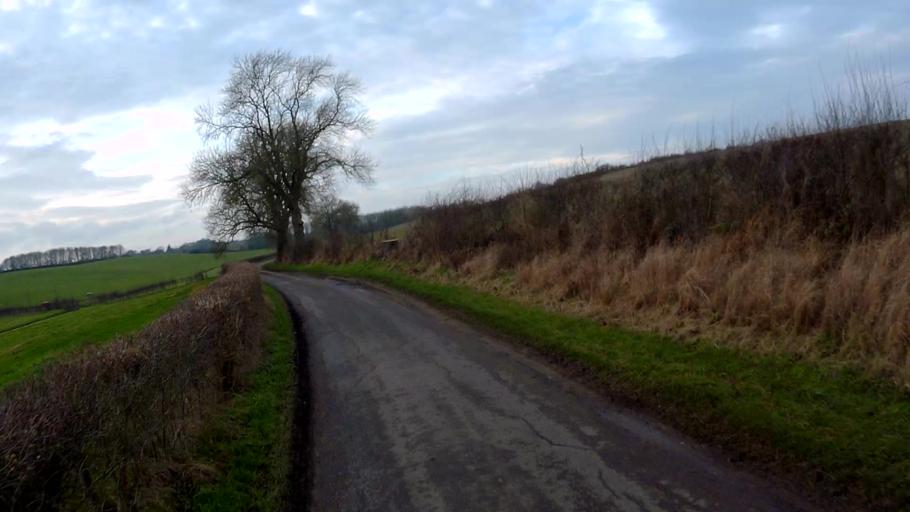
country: GB
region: England
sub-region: Lincolnshire
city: Bourne
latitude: 52.8281
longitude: -0.4640
